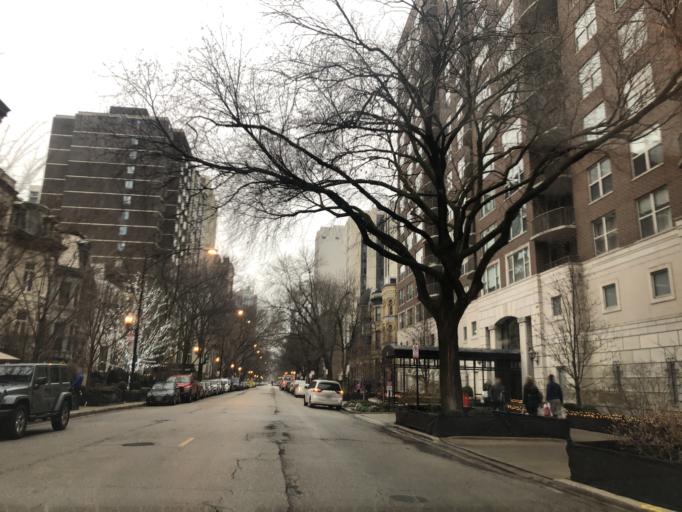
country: US
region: Illinois
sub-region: Cook County
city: Chicago
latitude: 41.9057
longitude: -87.6300
